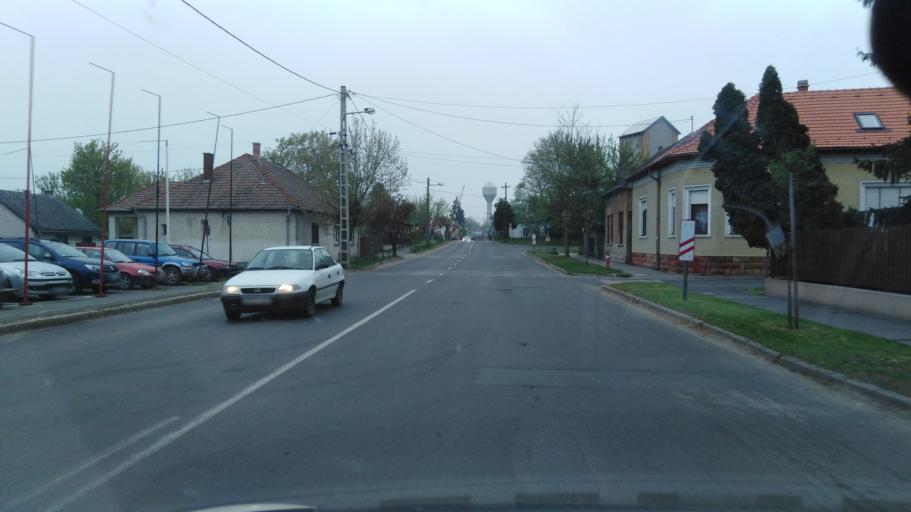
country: HU
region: Nograd
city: Balassagyarmat
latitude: 48.0732
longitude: 19.2963
